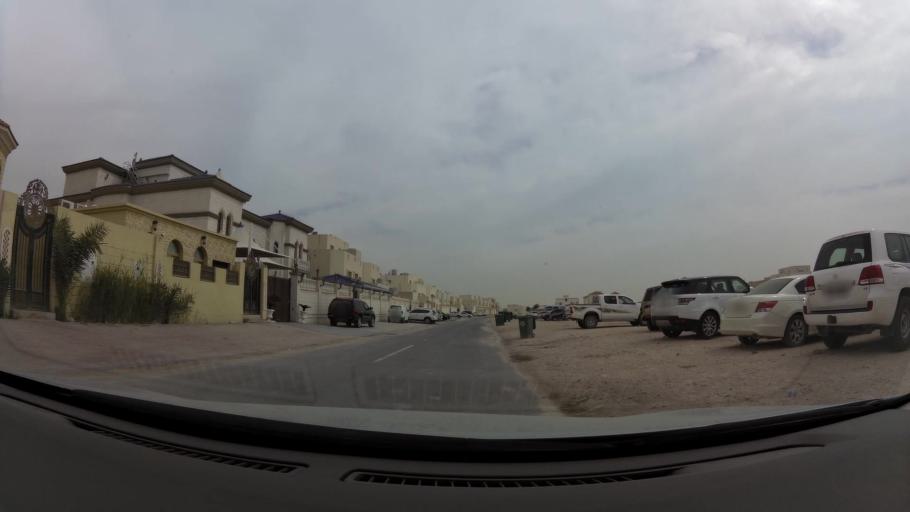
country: QA
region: Baladiyat ar Rayyan
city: Ar Rayyan
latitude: 25.2143
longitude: 51.4483
